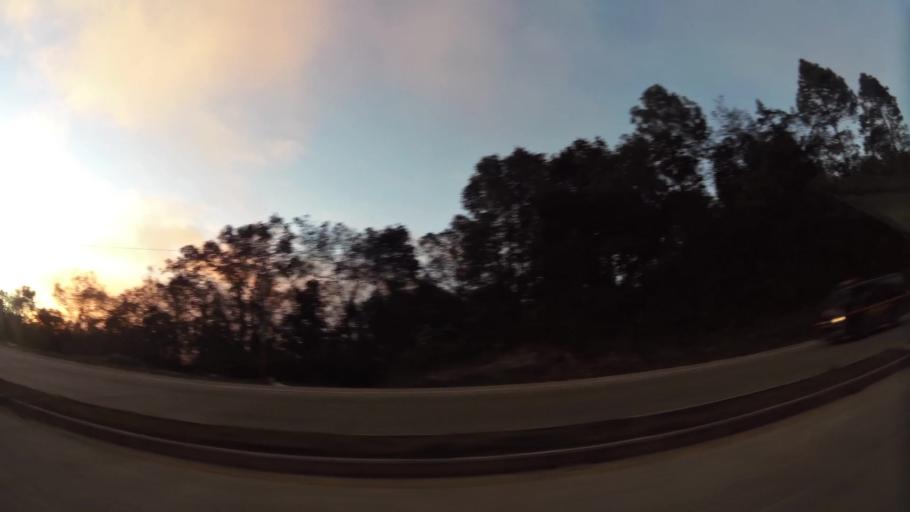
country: GT
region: Solola
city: Concepcion
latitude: 14.8359
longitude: -91.1101
